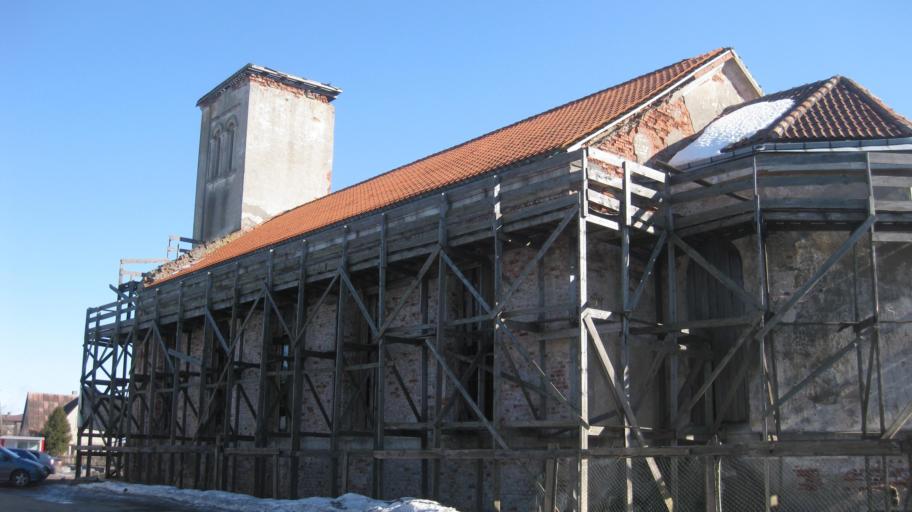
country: LT
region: Kauno apskritis
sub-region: Kauno rajonas
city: Garliava
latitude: 54.8258
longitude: 23.8715
